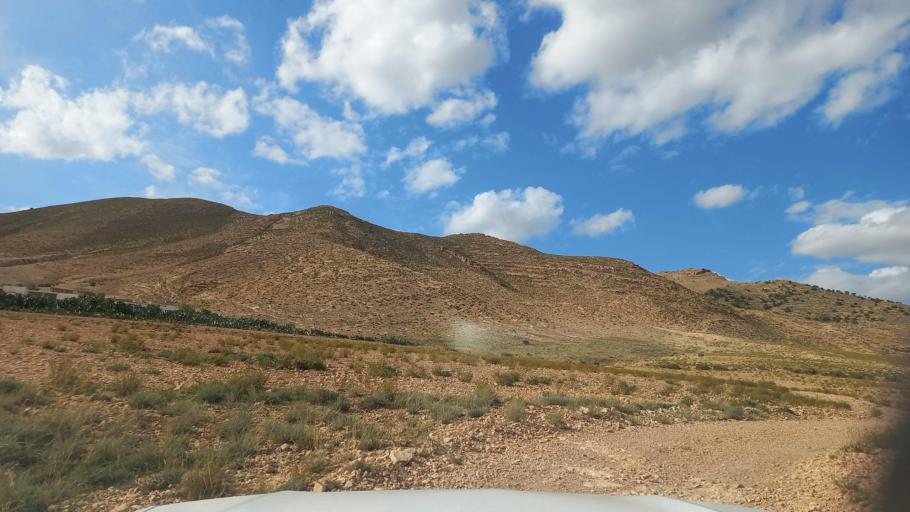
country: TN
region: Al Qasrayn
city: Sbiba
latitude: 35.4564
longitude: 9.0698
